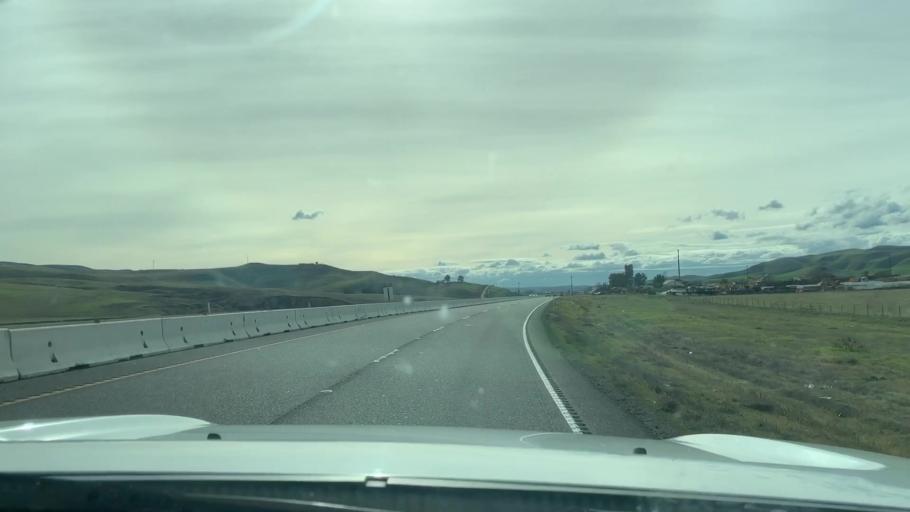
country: US
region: California
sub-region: San Luis Obispo County
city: Shandon
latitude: 35.6988
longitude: -120.3244
